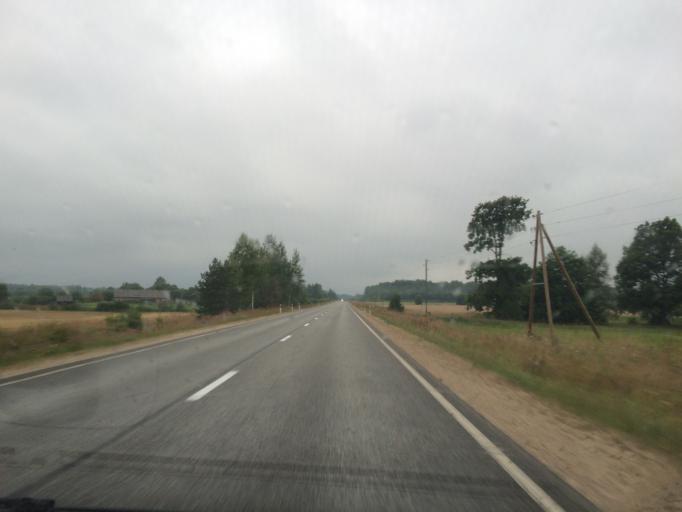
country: LV
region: Livani
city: Livani
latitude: 56.5217
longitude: 26.4463
